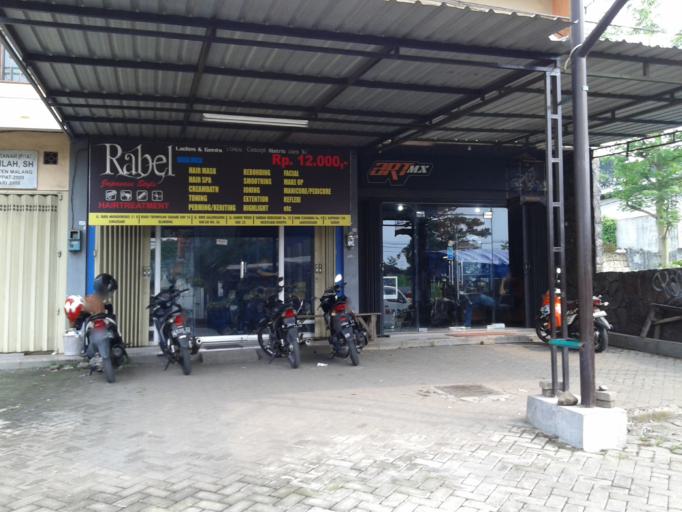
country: ID
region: East Java
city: Singosari
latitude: -7.9088
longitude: 112.6586
